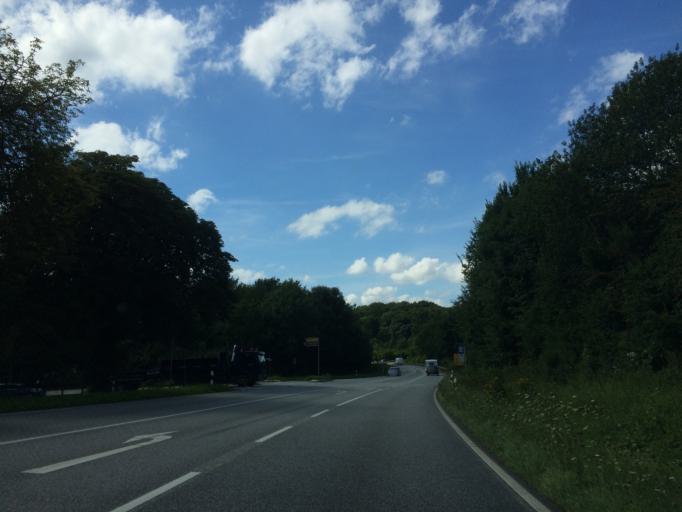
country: DE
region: Schleswig-Holstein
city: Bosdorf
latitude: 54.1405
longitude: 10.4819
